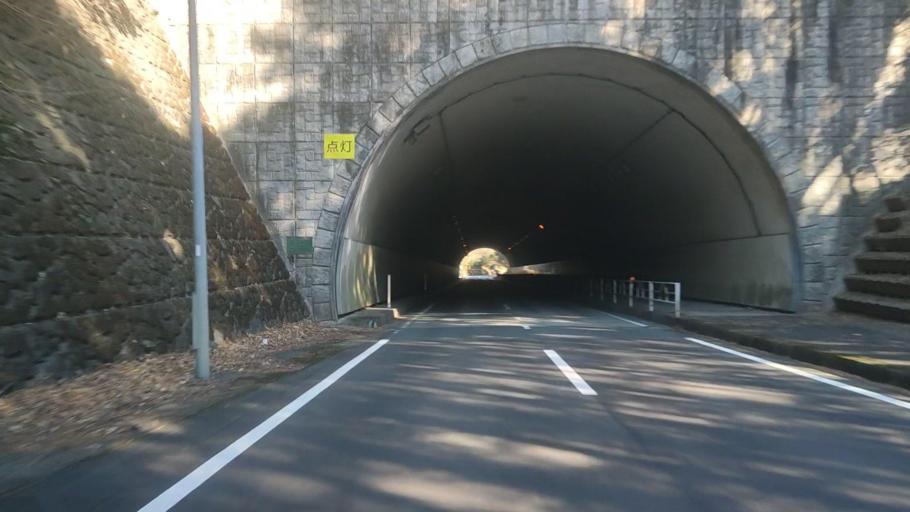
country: JP
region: Miyazaki
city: Nobeoka
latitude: 32.7017
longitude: 131.8153
